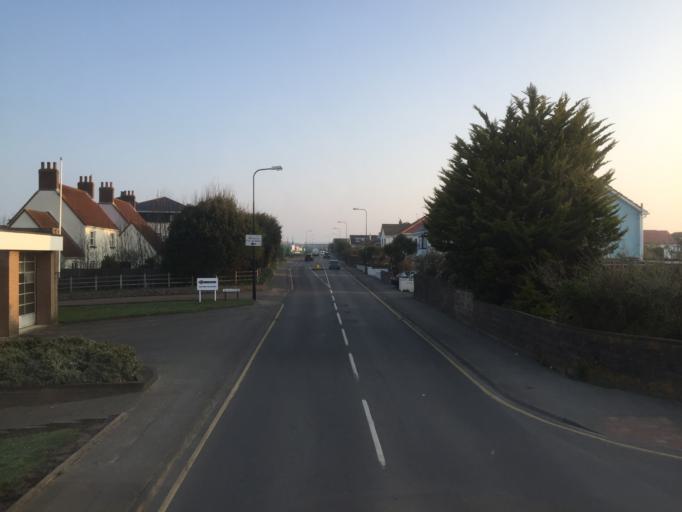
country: JE
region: St Helier
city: Saint Helier
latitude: 49.1962
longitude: -2.1982
